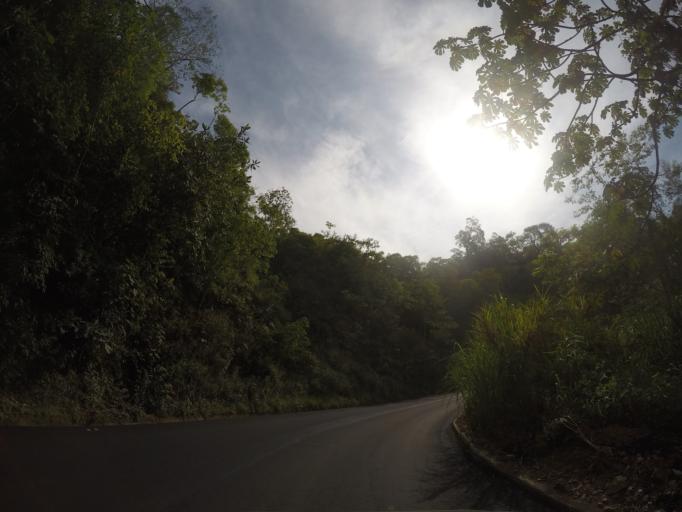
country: MX
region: Oaxaca
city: Pluma Hidalgo
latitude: 15.9327
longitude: -96.4280
